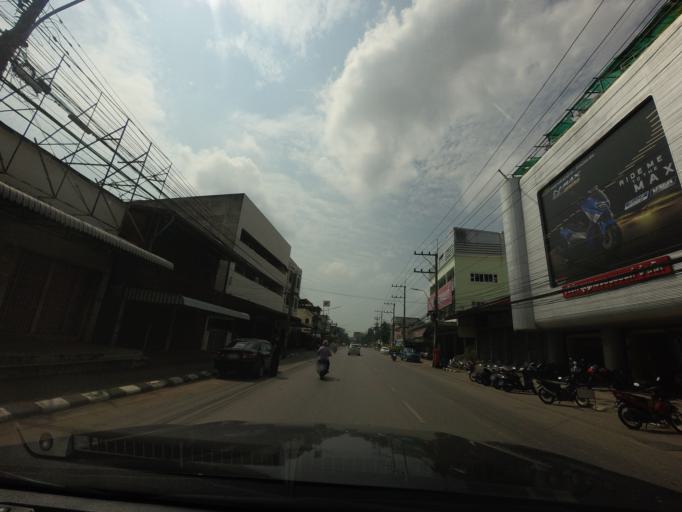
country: TH
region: Phrae
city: Phrae
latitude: 18.1441
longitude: 100.1487
